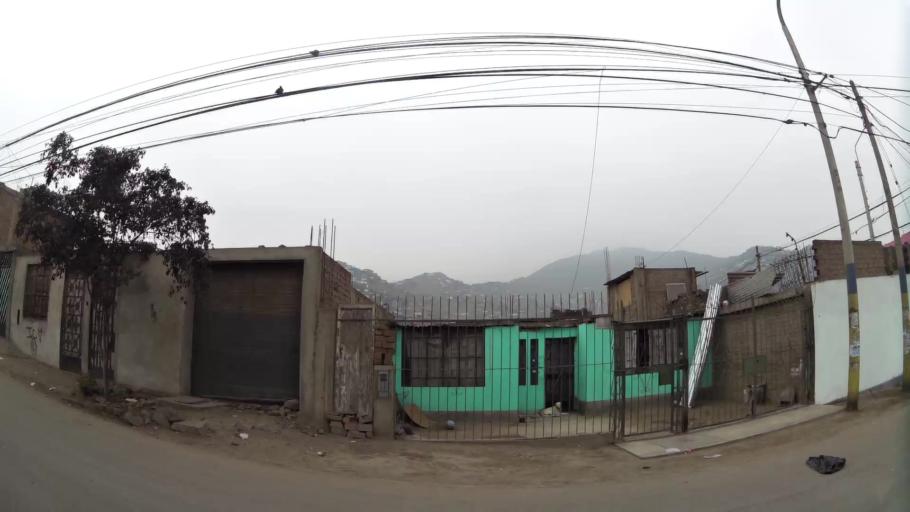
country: PE
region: Lima
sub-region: Lima
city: Urb. Santo Domingo
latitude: -11.9400
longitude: -76.9716
